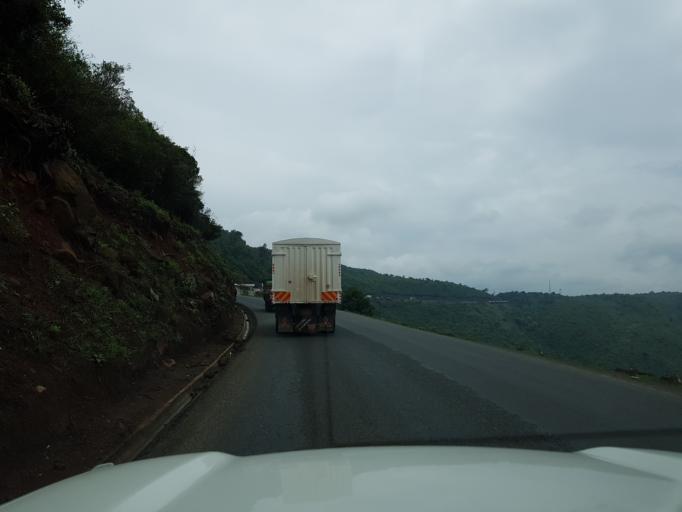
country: KE
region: Kiambu
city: Limuru
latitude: -1.0538
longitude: 36.6017
